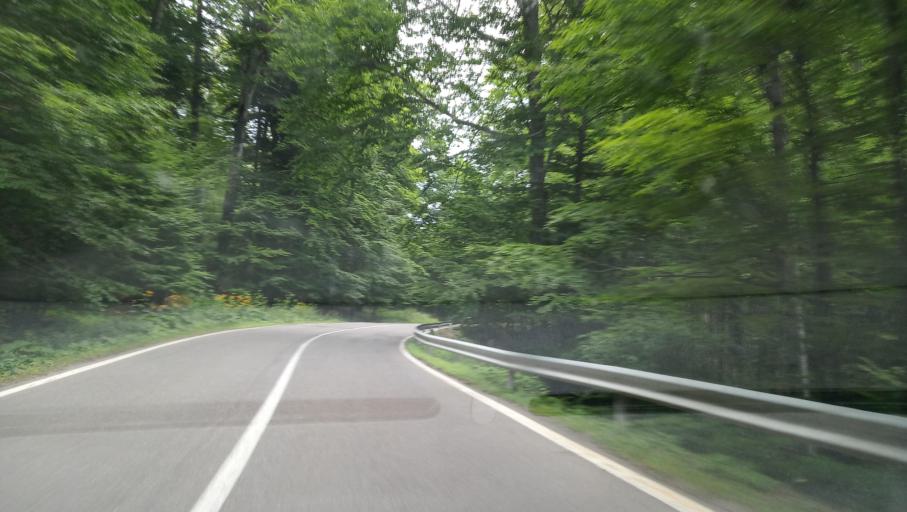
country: RO
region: Prahova
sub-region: Oras Sinaia
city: Sinaia
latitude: 45.3177
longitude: 25.5199
